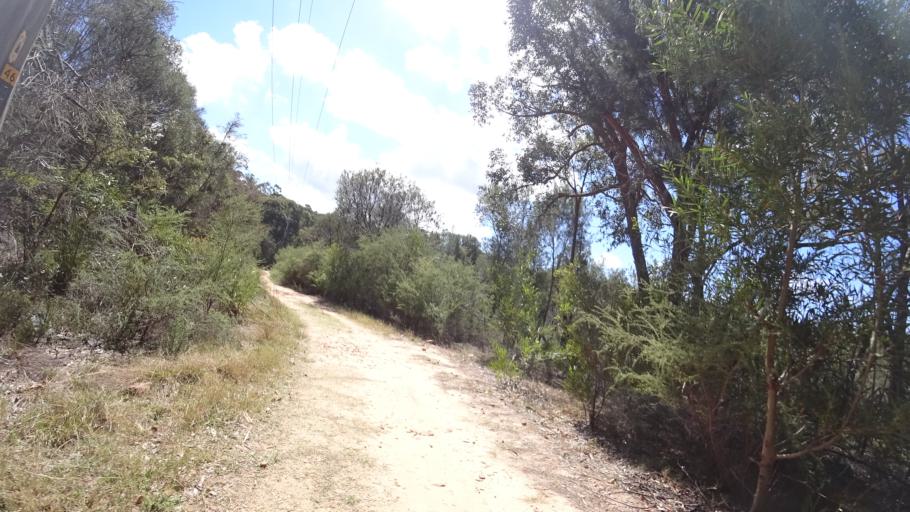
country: AU
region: New South Wales
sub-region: Warringah
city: Killarney Heights
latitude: -33.7636
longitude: 151.2222
